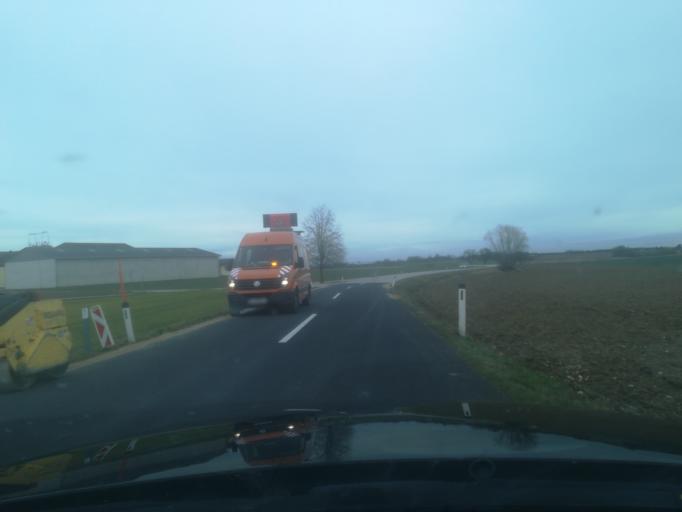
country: AT
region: Upper Austria
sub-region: Wels-Land
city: Steinhaus
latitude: 48.1229
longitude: 13.9955
